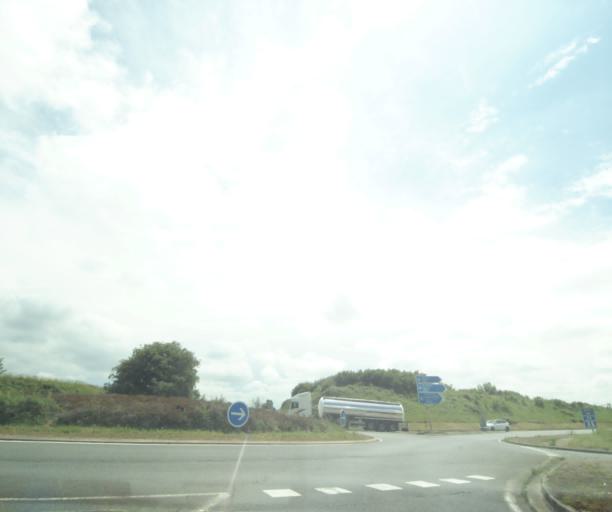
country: FR
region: Poitou-Charentes
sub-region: Departement des Deux-Sevres
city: Echire
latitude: 46.4229
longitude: -0.3967
